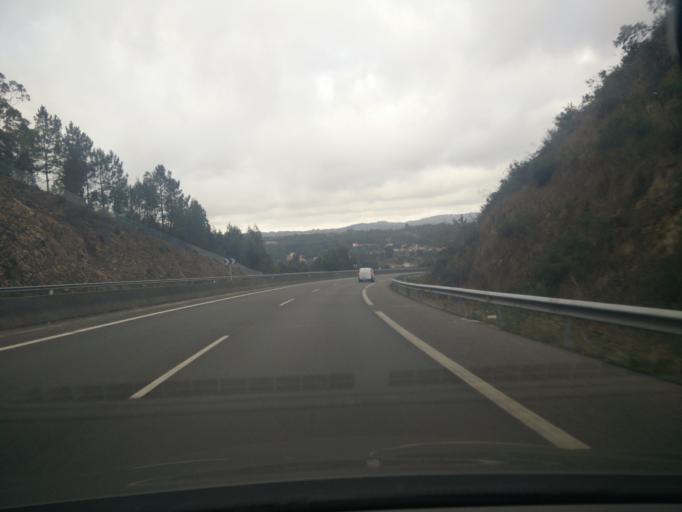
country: ES
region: Galicia
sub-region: Provincia da Coruna
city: Arteixo
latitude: 43.2890
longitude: -8.5040
